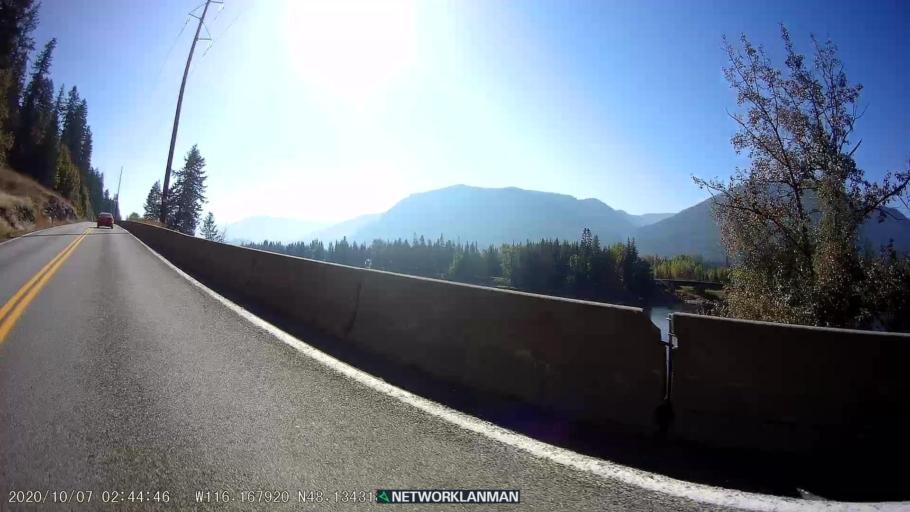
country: US
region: Idaho
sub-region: Bonner County
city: Ponderay
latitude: 48.1343
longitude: -116.1677
